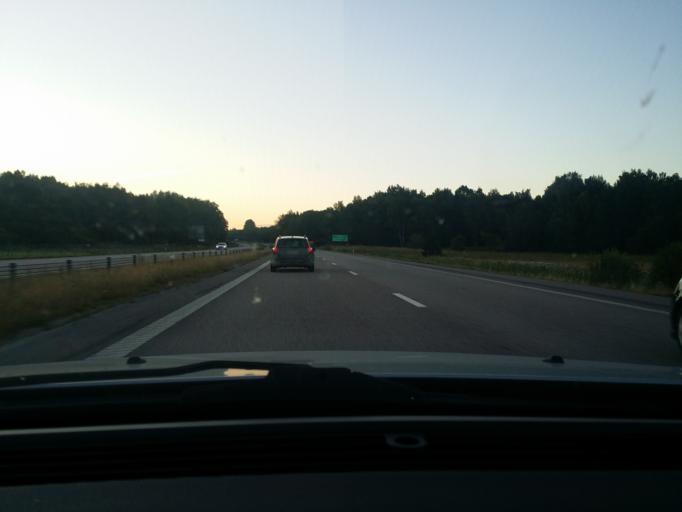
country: SE
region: Uppsala
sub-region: Enkopings Kommun
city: Enkoping
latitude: 59.6537
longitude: 17.0940
